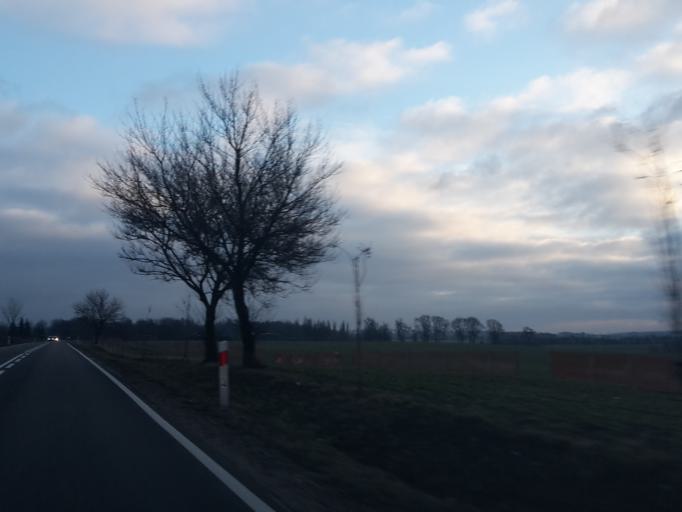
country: PL
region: Warmian-Masurian Voivodeship
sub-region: Powiat ilawski
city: Lubawa
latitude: 53.5910
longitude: 19.8487
